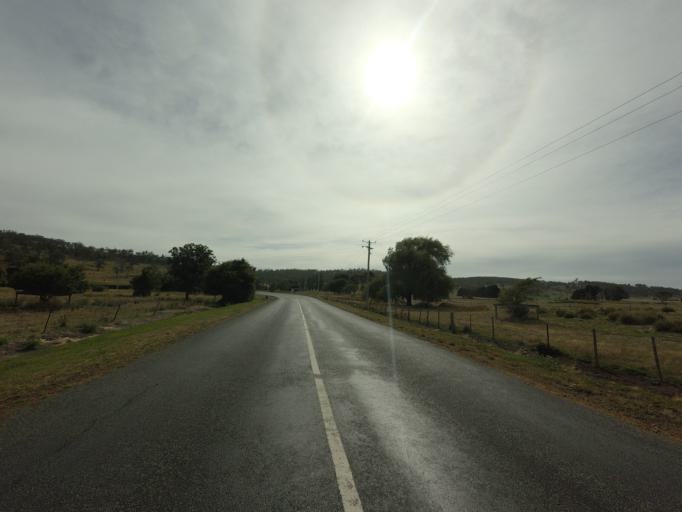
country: AU
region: Tasmania
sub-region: Brighton
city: Bridgewater
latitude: -42.2956
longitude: 147.3849
